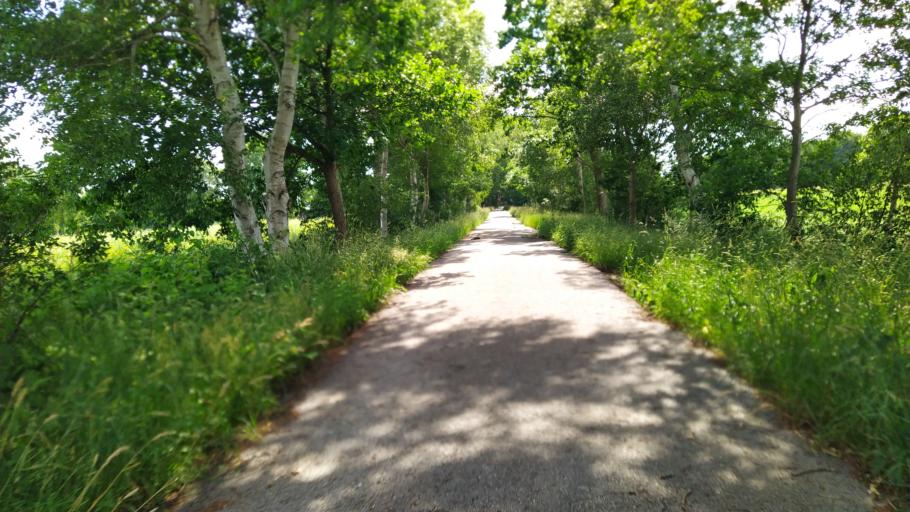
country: DE
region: Lower Saxony
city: Stinstedt
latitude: 53.6497
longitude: 8.9450
